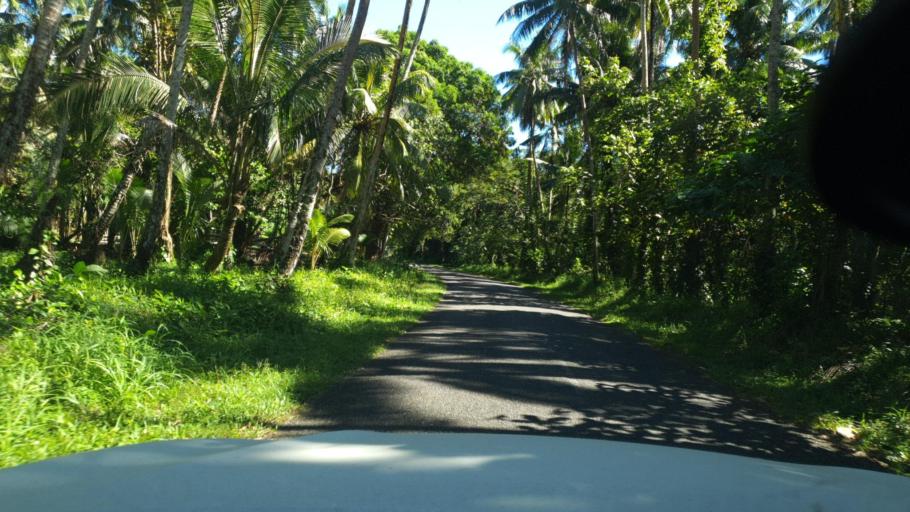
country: SB
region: Guadalcanal
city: Honiara
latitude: -9.2781
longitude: 159.7382
